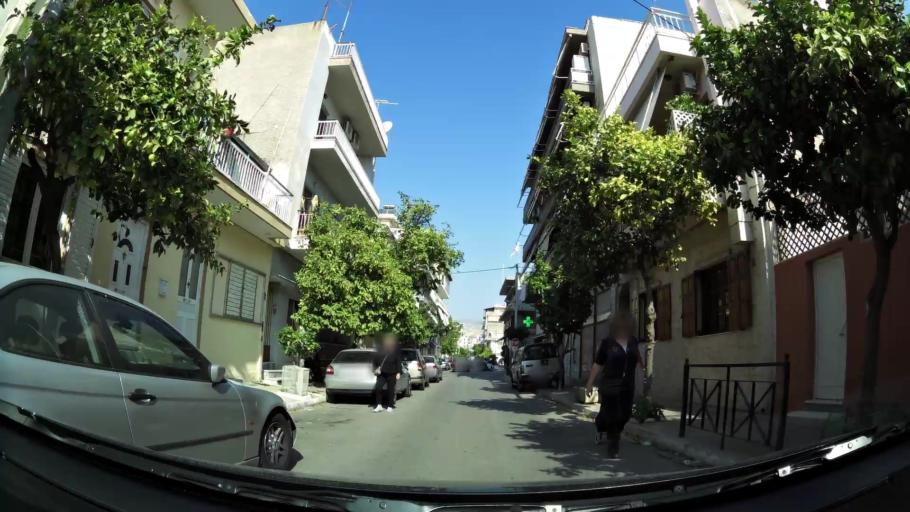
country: GR
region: Attica
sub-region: Nomos Piraios
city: Drapetsona
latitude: 37.9500
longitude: 23.6300
